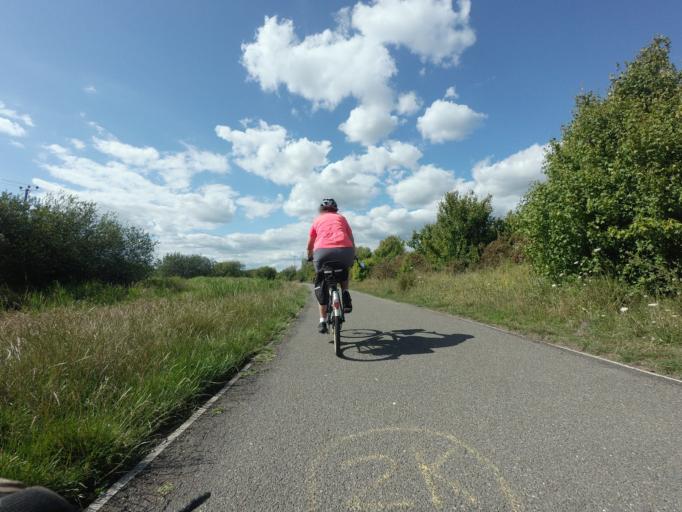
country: GB
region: England
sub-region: East Sussex
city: Eastbourne
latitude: 50.8016
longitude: 0.2894
